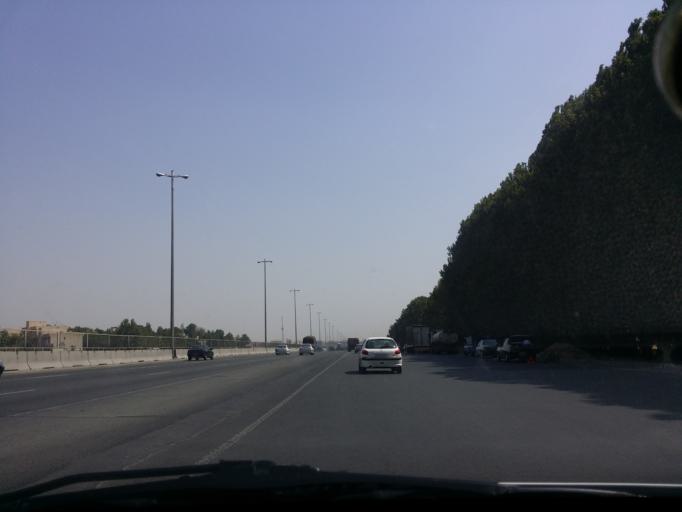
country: IR
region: Alborz
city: Karaj
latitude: 35.8460
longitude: 50.9092
